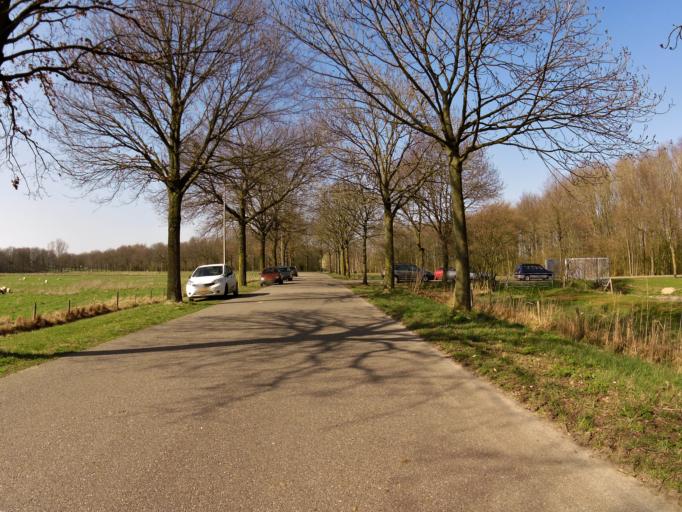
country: NL
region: Gelderland
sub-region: Gemeente Maasdriel
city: Hedel
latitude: 51.7007
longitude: 5.2413
